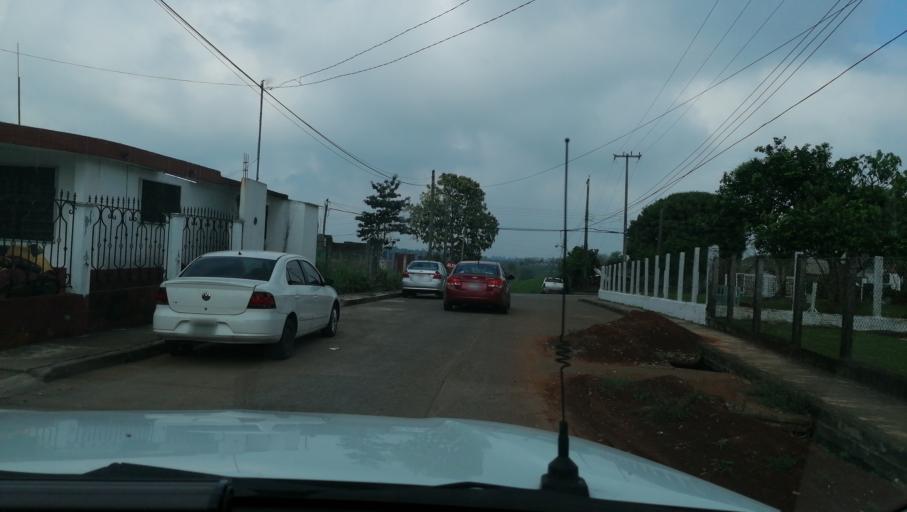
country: MX
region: Chiapas
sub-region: Juarez
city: El Triunfo 1ra. Seccion (Cardona)
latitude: 17.6086
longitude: -93.1938
